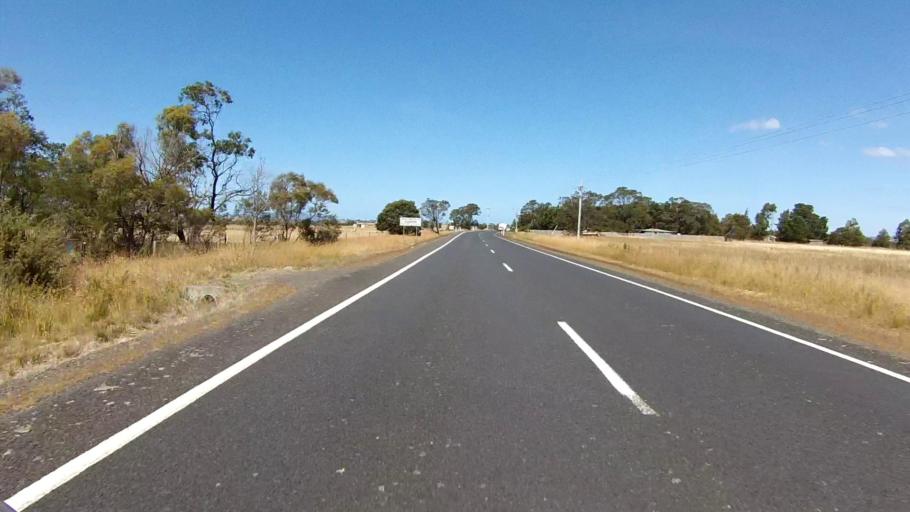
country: AU
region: Tasmania
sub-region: Break O'Day
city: St Helens
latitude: -42.0576
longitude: 148.0597
